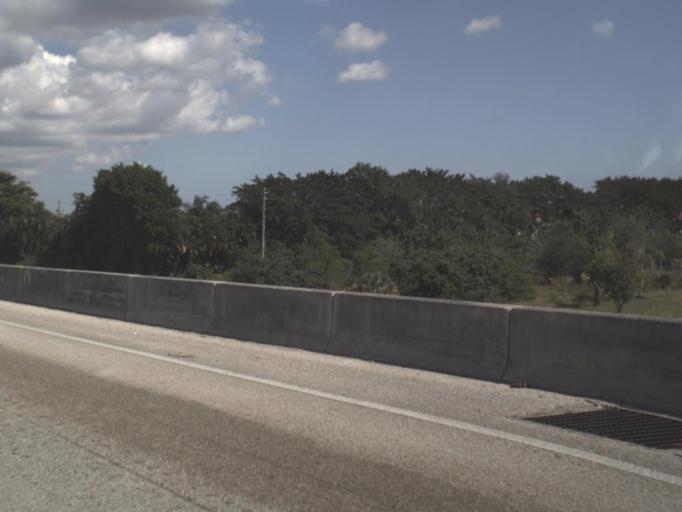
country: US
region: Florida
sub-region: Palm Beach County
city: Villages of Oriole
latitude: 26.5294
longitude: -80.1725
